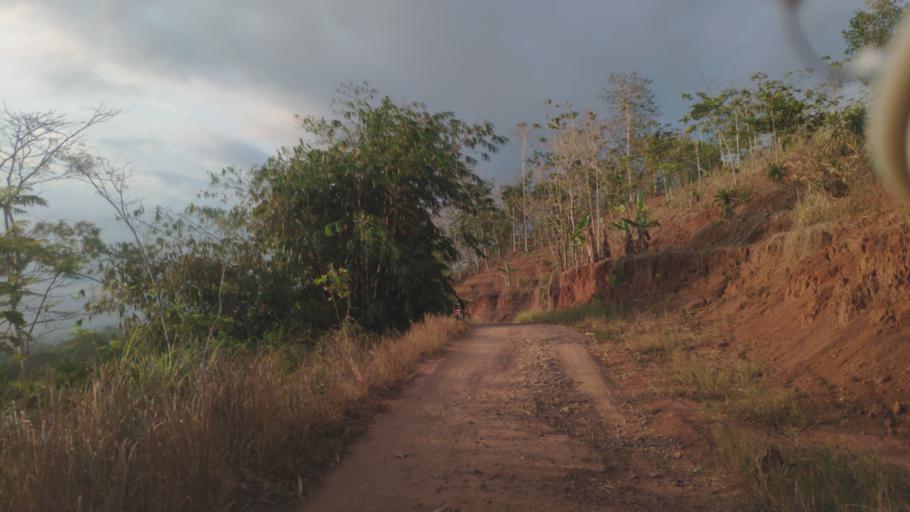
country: ID
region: Central Java
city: Purbalingga
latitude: -7.3442
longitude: 109.5321
